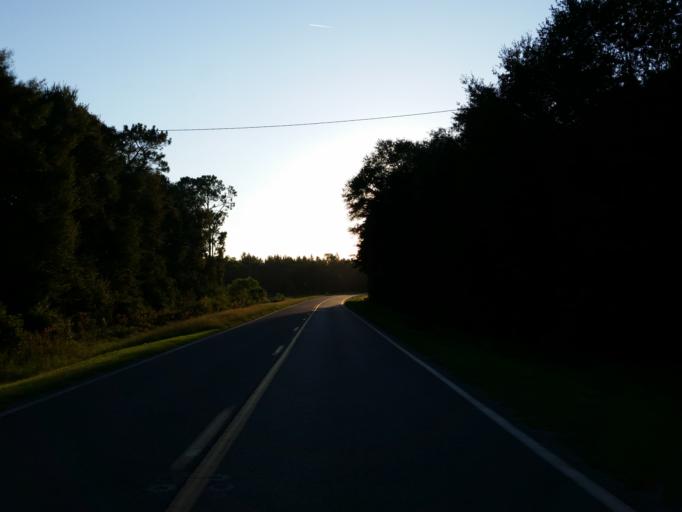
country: US
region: Georgia
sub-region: Berrien County
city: Nashville
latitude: 31.1794
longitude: -83.1345
